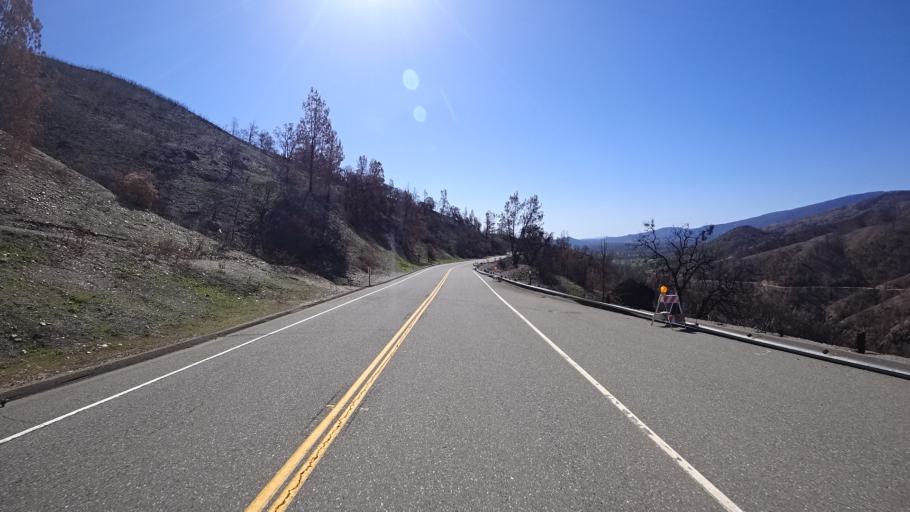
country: US
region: California
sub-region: Glenn County
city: Orland
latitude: 39.6421
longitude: -122.6063
